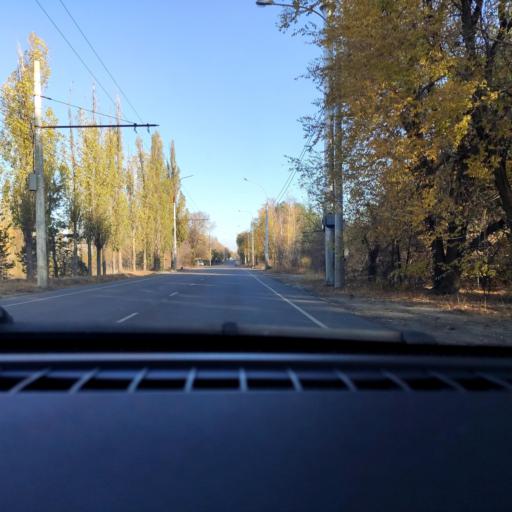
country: RU
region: Voronezj
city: Somovo
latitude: 51.7113
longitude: 39.2926
